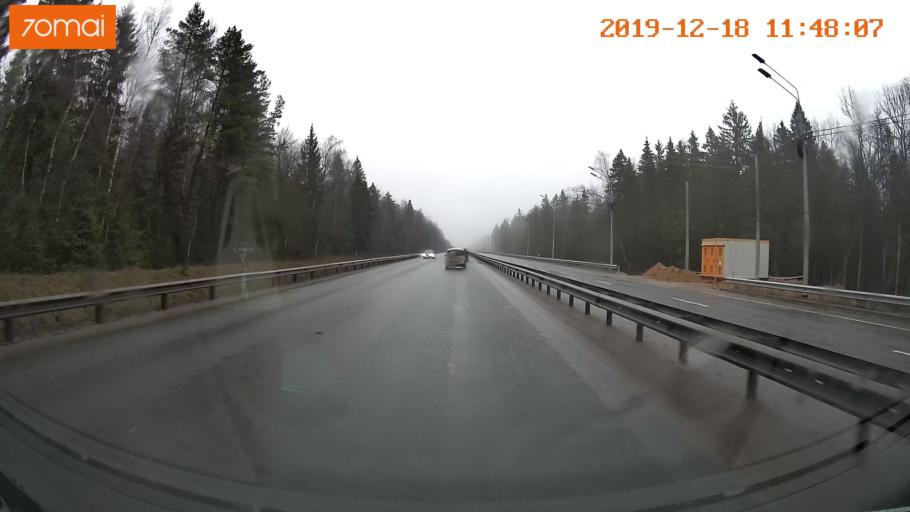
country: RU
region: Moskovskaya
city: Yershovo
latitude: 55.7647
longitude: 36.9006
